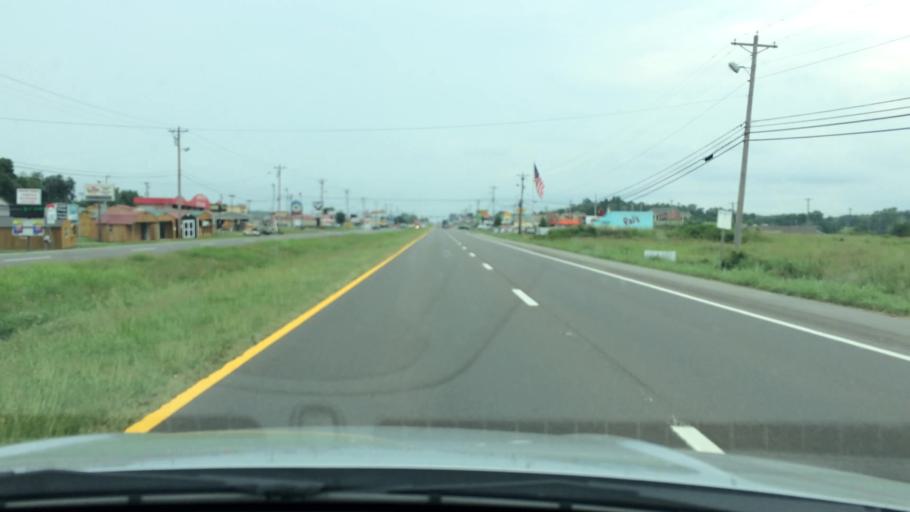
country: US
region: Tennessee
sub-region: Jefferson County
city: Jefferson City
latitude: 36.1232
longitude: -83.4731
